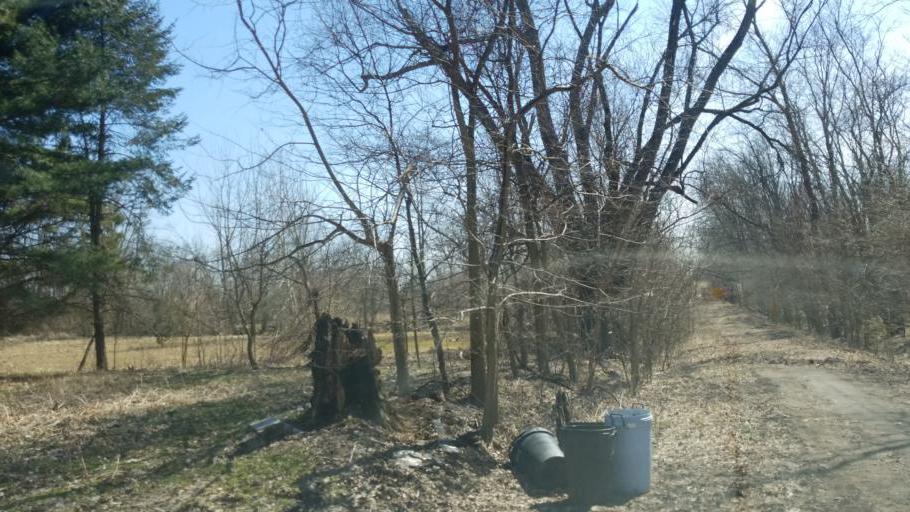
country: US
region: Ohio
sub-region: Morrow County
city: Cardington
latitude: 40.6342
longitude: -82.9425
